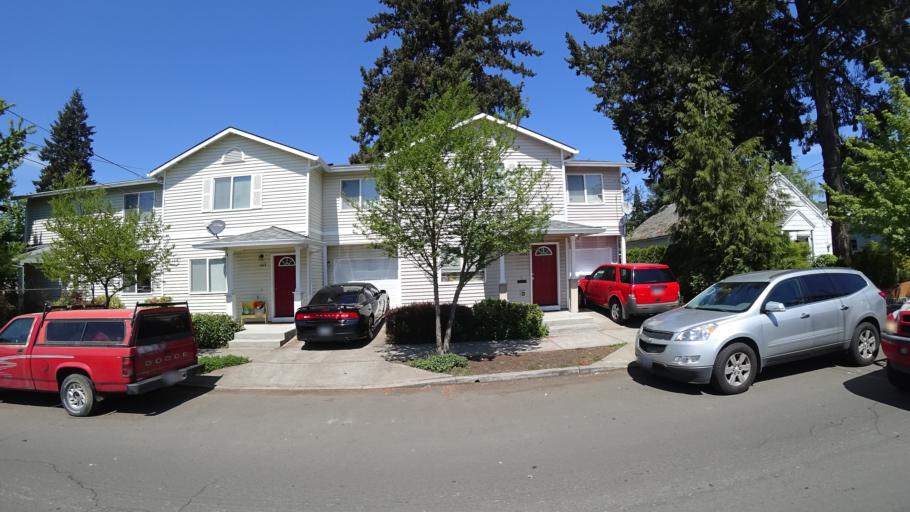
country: US
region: Oregon
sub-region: Washington County
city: Hillsboro
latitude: 45.5173
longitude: -122.9675
